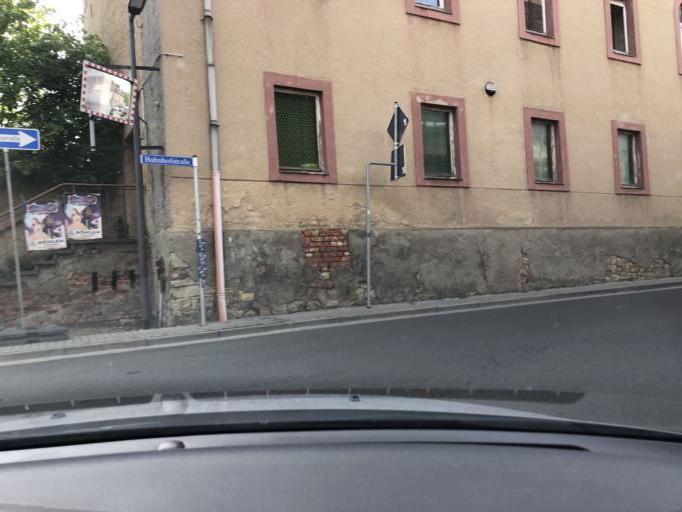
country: DE
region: Saxony
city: Rotha
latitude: 51.1983
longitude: 12.4099
